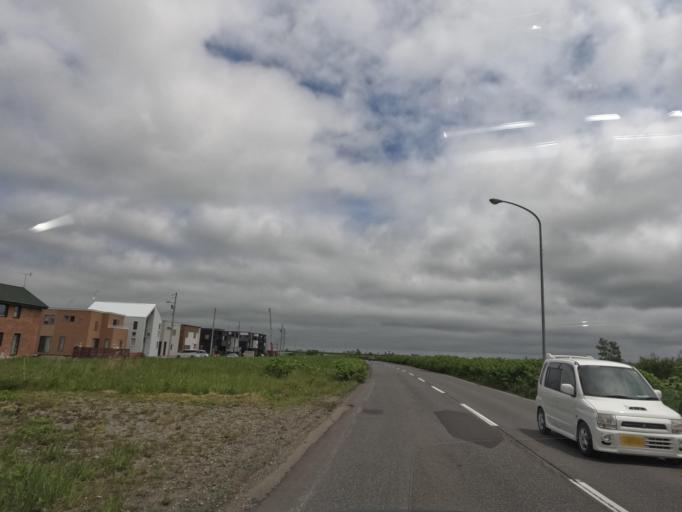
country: JP
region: Hokkaido
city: Sapporo
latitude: 43.0911
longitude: 141.4322
